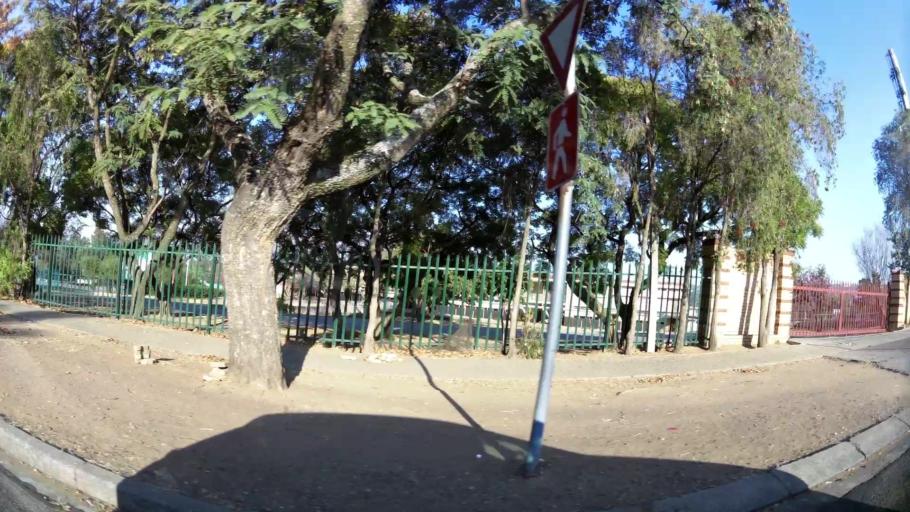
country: ZA
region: Gauteng
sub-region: City of Johannesburg Metropolitan Municipality
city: Modderfontein
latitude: -26.1387
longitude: 28.1161
